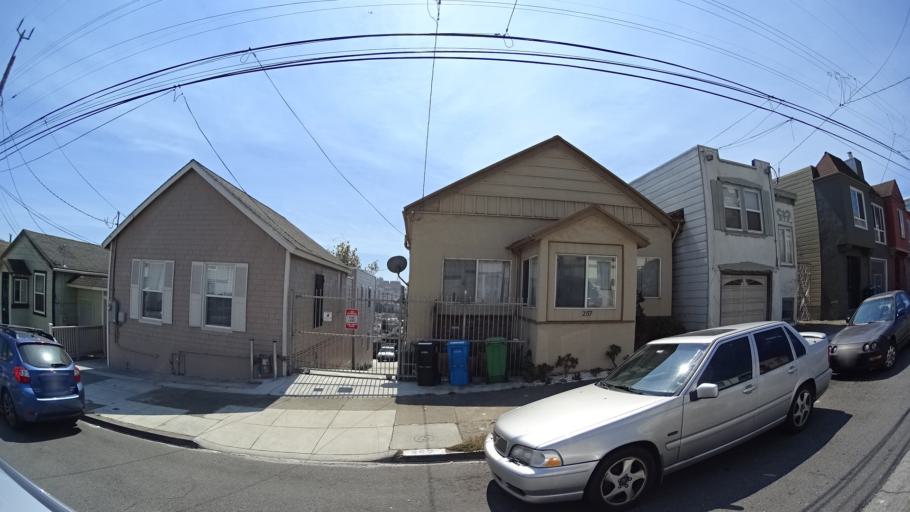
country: US
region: California
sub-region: San Mateo County
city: Daly City
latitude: 37.7166
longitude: -122.4610
